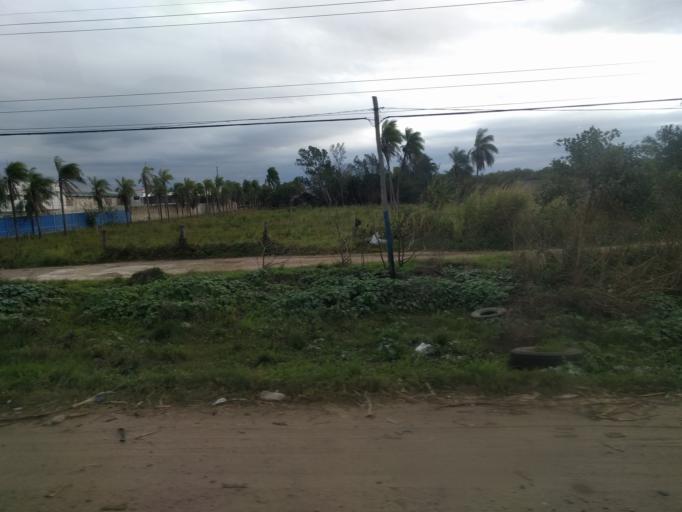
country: BO
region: Santa Cruz
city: La Belgica
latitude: -17.6141
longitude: -63.1595
